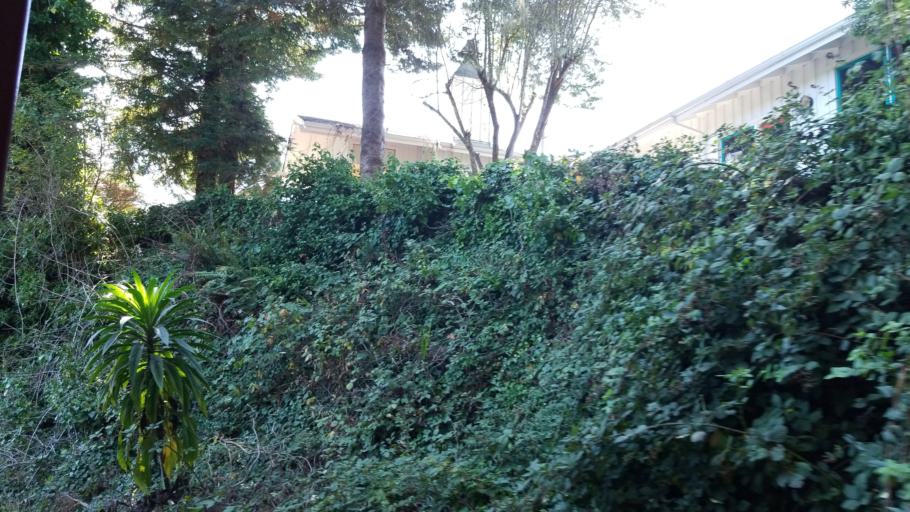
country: US
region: California
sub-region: Mendocino County
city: Fort Bragg
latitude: 39.4510
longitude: -123.8005
